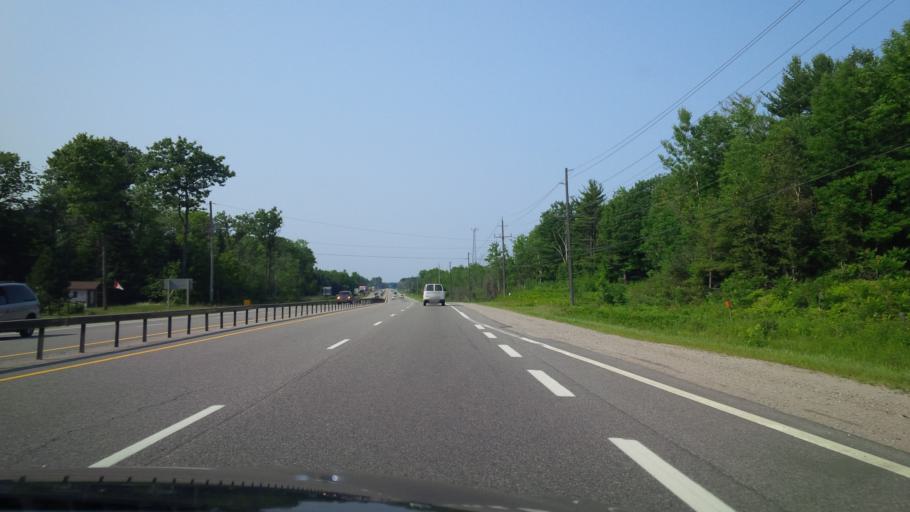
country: CA
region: Ontario
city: Orillia
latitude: 44.7223
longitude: -79.3764
